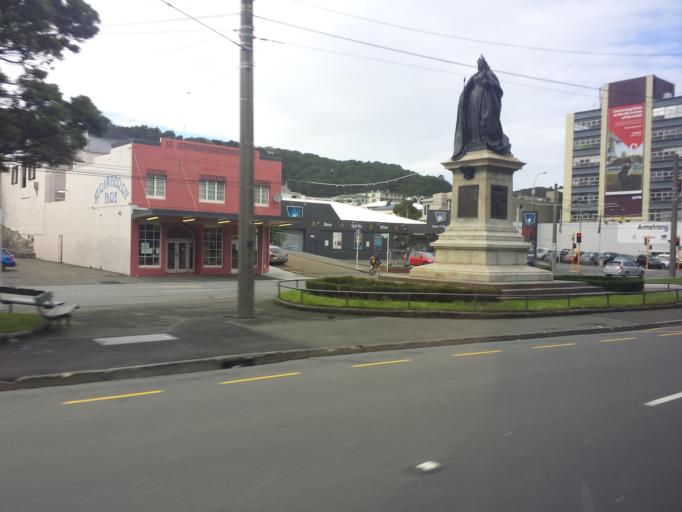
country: NZ
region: Wellington
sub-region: Wellington City
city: Wellington
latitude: -41.2950
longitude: 174.7830
